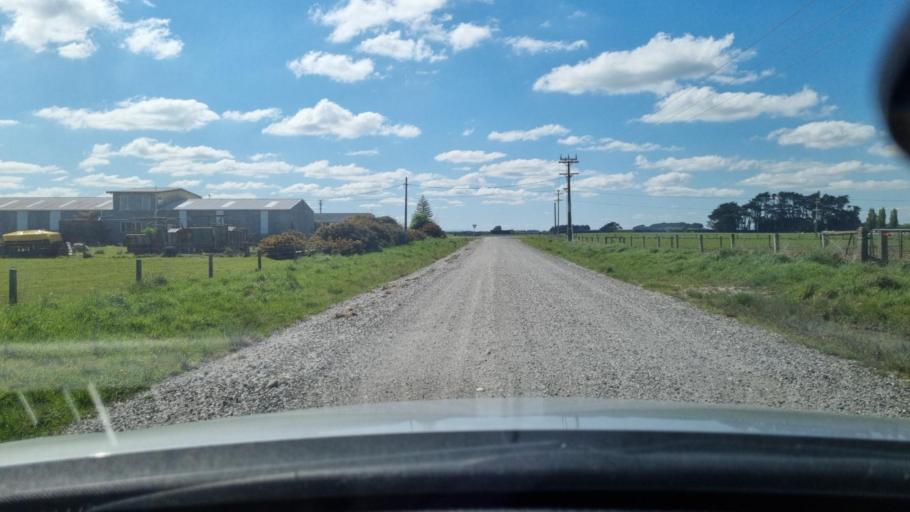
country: NZ
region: Southland
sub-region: Invercargill City
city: Invercargill
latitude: -46.3707
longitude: 168.2985
